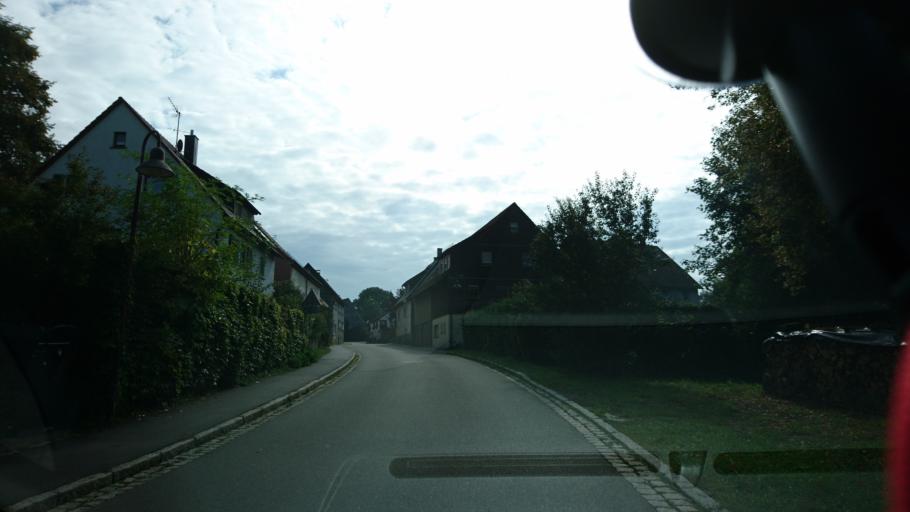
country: DE
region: Baden-Wuerttemberg
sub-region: Regierungsbezirk Stuttgart
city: Mainhardt
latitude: 49.1032
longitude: 9.5674
